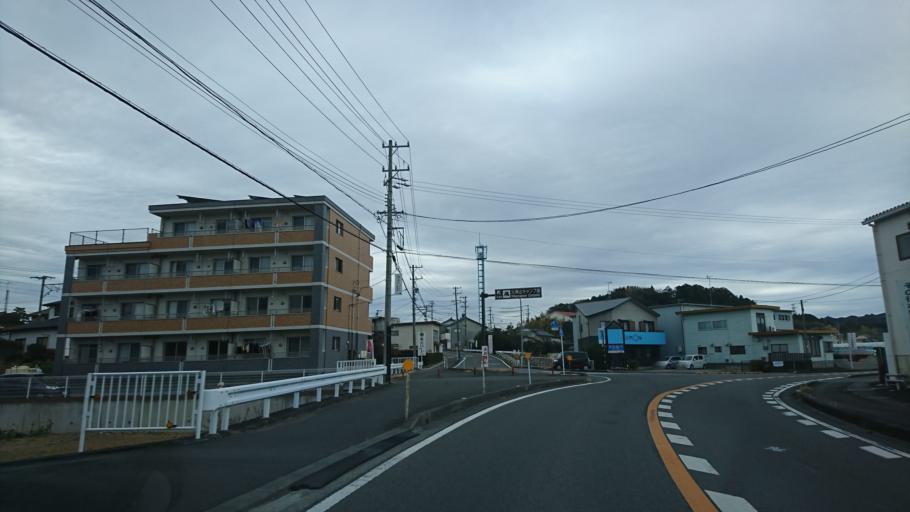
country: JP
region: Shizuoka
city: Kanaya
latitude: 34.7716
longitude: 138.1092
